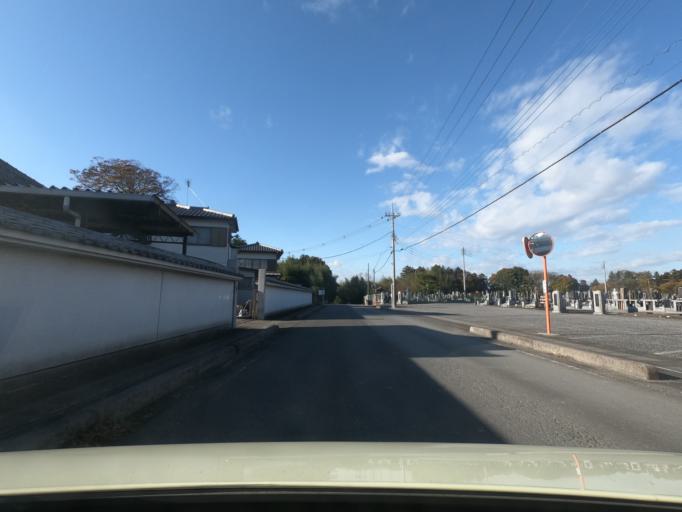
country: JP
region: Ibaraki
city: Koga
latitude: 36.2441
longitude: 139.7362
